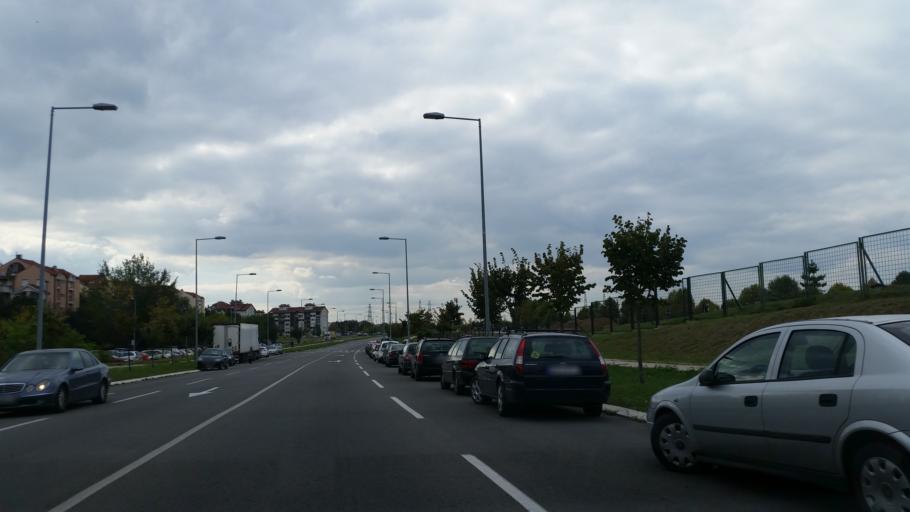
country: RS
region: Central Serbia
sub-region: Belgrade
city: Zemun
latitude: 44.8131
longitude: 20.3671
